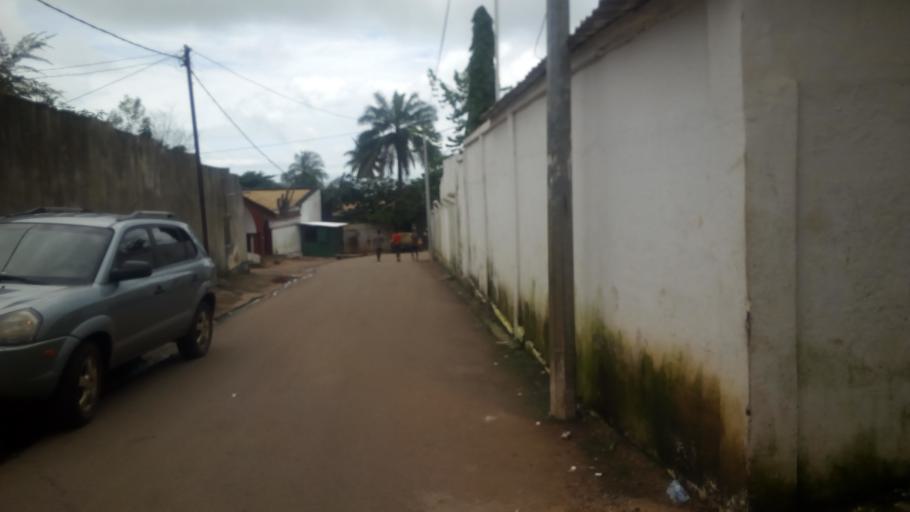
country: GN
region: Conakry
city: Conakry
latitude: 9.5988
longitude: -13.6547
